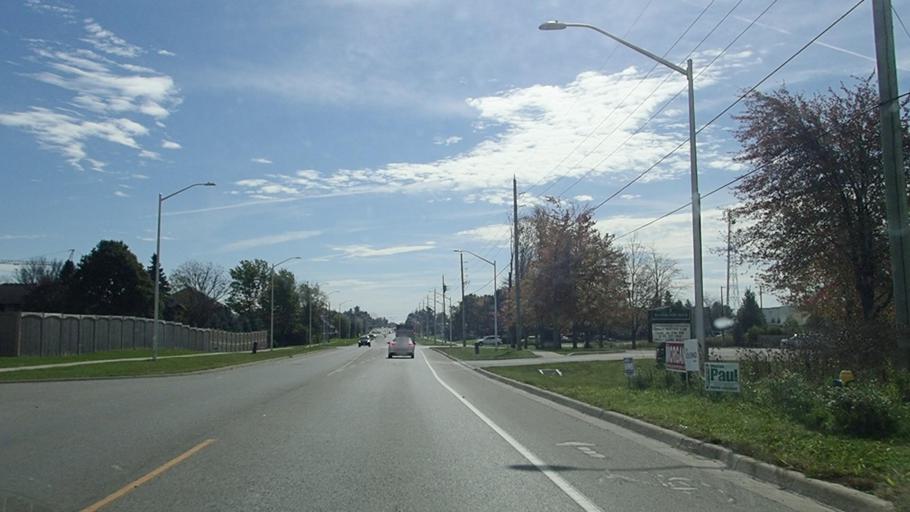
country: CA
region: Ontario
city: London
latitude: 43.0236
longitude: -81.3133
